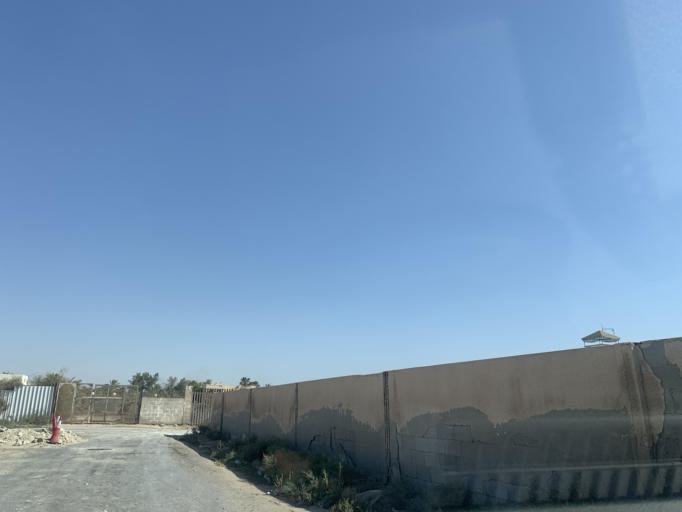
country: BH
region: Northern
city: Madinat `Isa
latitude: 26.1893
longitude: 50.4687
